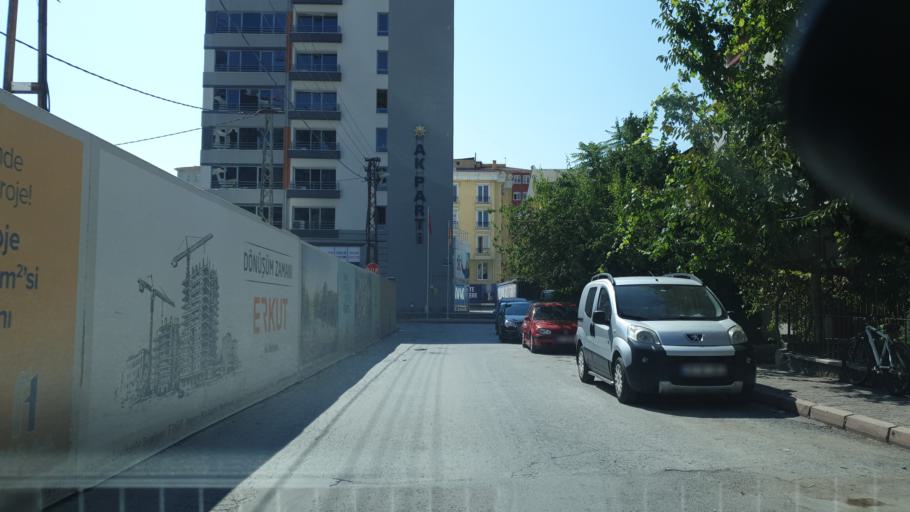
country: TR
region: Kayseri
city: Kayseri
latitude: 38.7270
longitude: 35.4903
